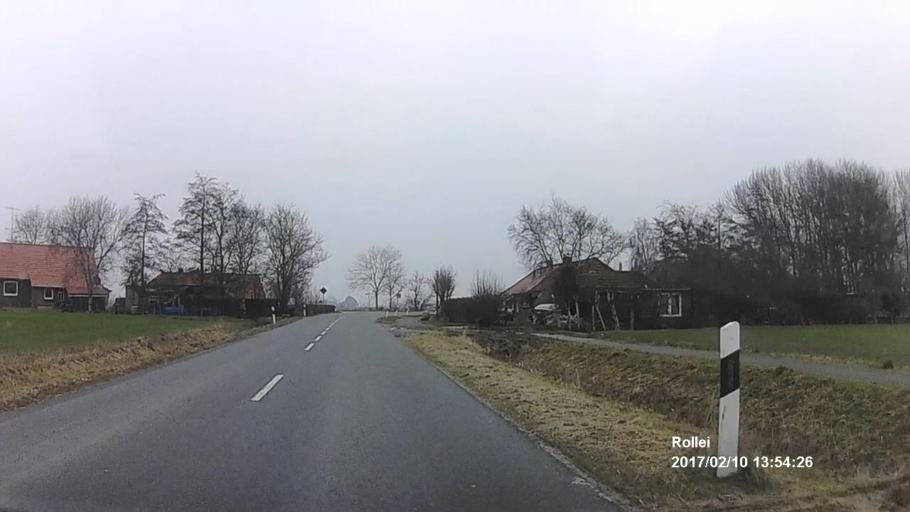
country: DE
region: Lower Saxony
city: Norddeich
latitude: 53.5667
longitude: 7.1390
